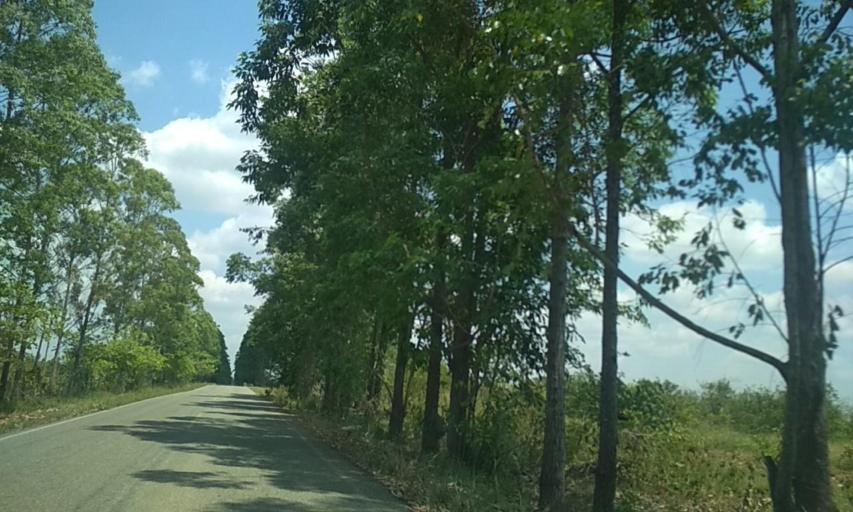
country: MX
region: Tabasco
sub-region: Huimanguillo
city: Francisco Rueda
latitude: 17.7653
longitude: -93.7937
